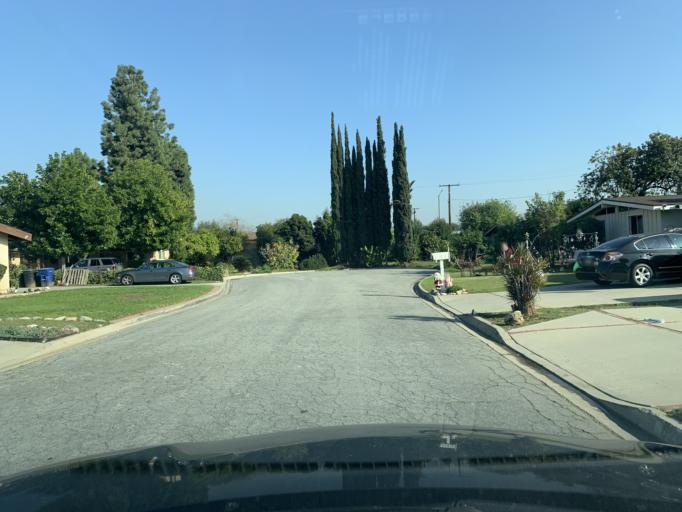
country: US
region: California
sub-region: Los Angeles County
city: Covina
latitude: 34.0776
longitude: -117.8997
